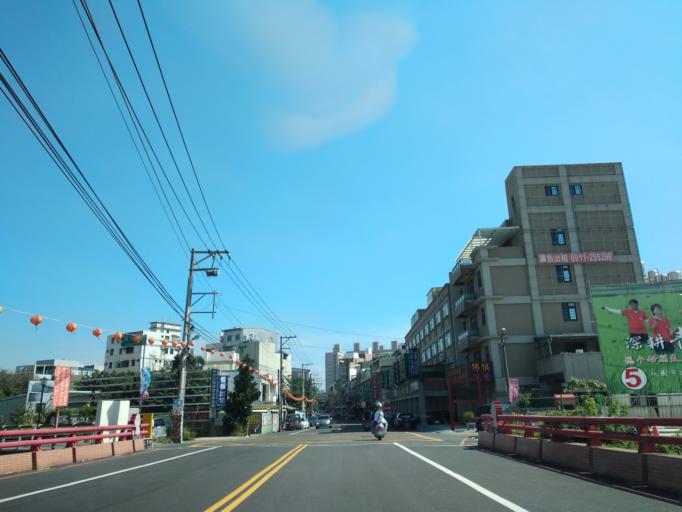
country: TW
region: Taiwan
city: Taoyuan City
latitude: 24.9471
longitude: 121.2109
